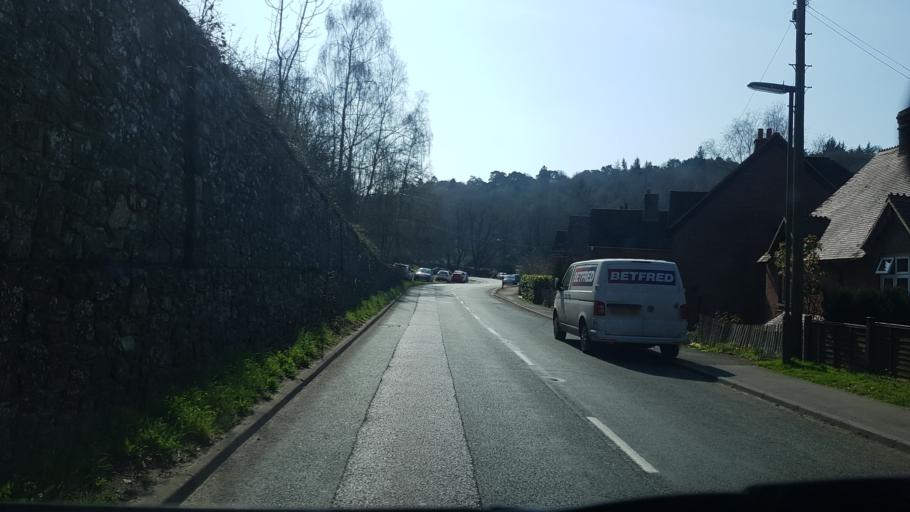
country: GB
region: England
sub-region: Surrey
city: Haslemere
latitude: 51.0823
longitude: -0.7304
